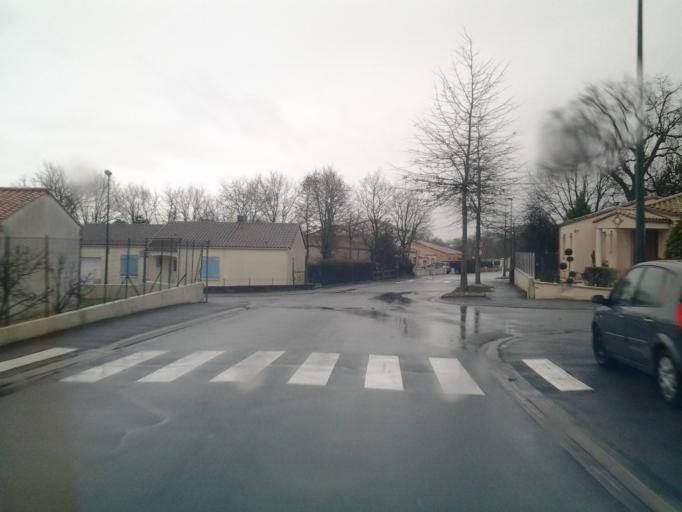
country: FR
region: Pays de la Loire
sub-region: Departement de la Vendee
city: La Roche-sur-Yon
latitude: 46.6781
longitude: -1.4471
